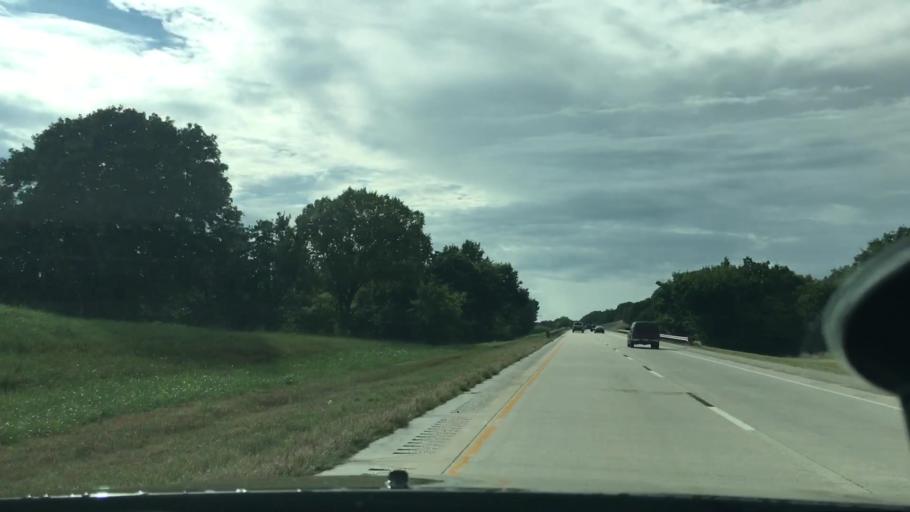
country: US
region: Oklahoma
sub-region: Okfuskee County
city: Boley
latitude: 35.3836
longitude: -96.5565
